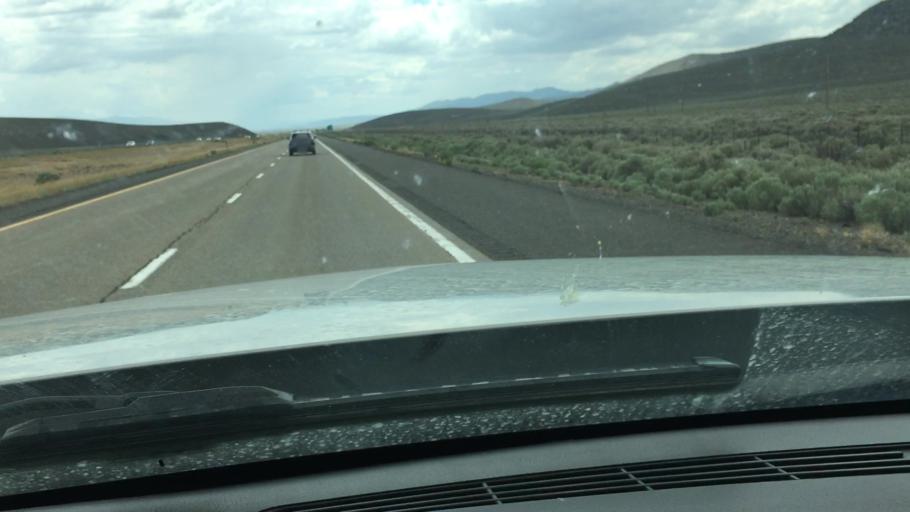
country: US
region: Utah
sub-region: Beaver County
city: Beaver
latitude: 38.0917
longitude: -112.6692
